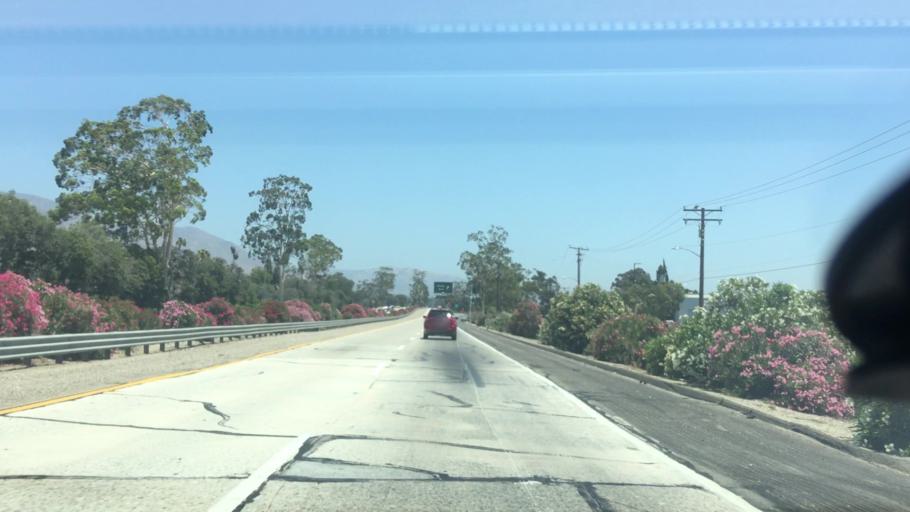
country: US
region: California
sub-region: Ventura County
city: Santa Paula
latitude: 34.3425
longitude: -119.0736
